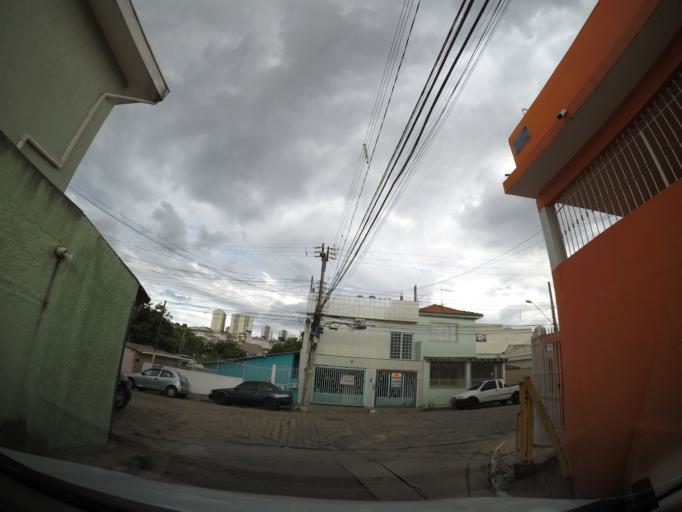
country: BR
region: Sao Paulo
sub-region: Guarulhos
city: Guarulhos
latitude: -23.4768
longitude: -46.5504
